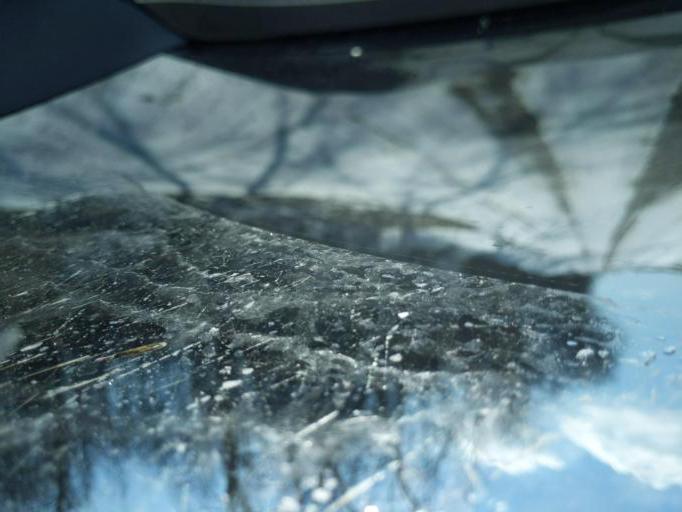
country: US
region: Michigan
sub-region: Livingston County
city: Fowlerville
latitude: 42.5371
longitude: -84.0882
